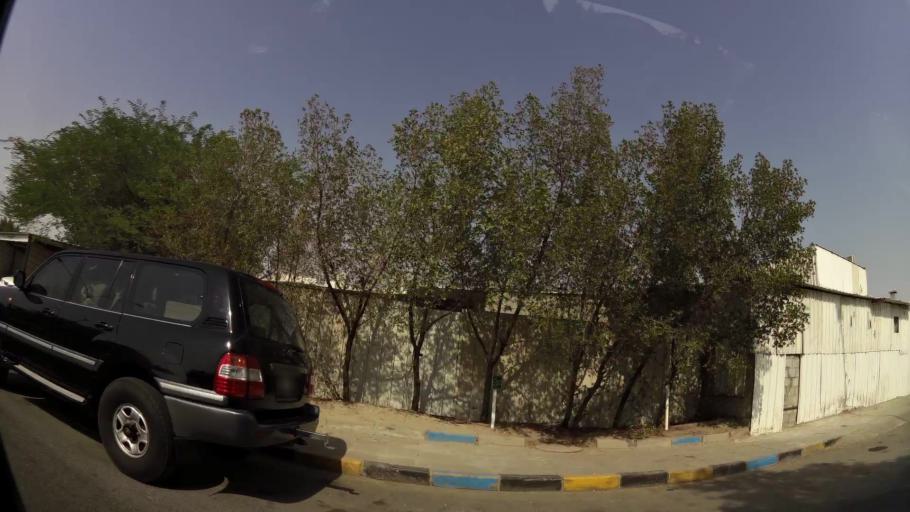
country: KW
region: Muhafazat al Jahra'
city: Al Jahra'
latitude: 29.3322
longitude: 47.6651
